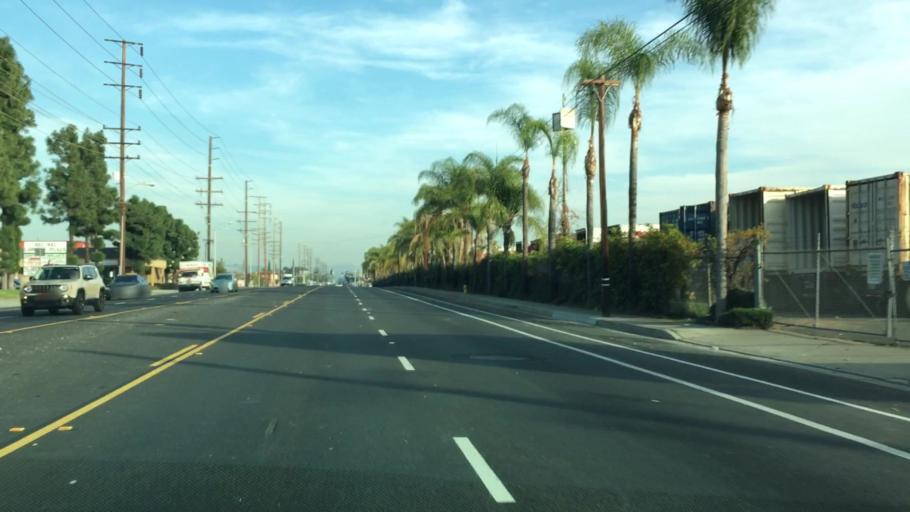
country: US
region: California
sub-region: Orange County
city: La Habra
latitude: 33.9246
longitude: -117.9372
